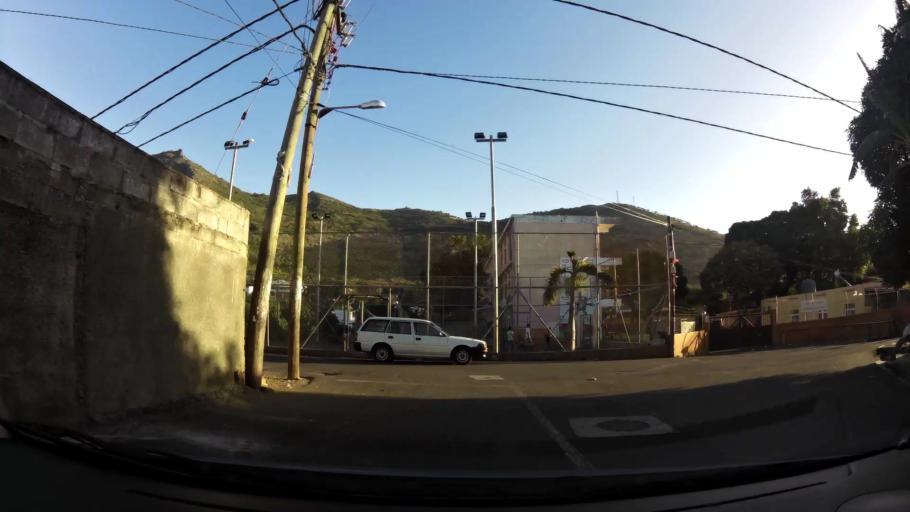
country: MU
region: Port Louis
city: Port Louis
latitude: -20.1771
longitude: 57.5131
